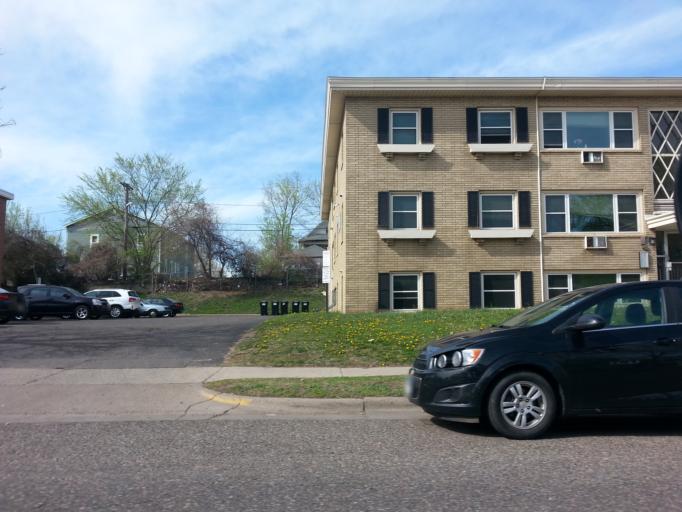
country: US
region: Minnesota
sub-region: Ramsey County
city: Saint Paul
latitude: 44.9630
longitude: -93.0754
